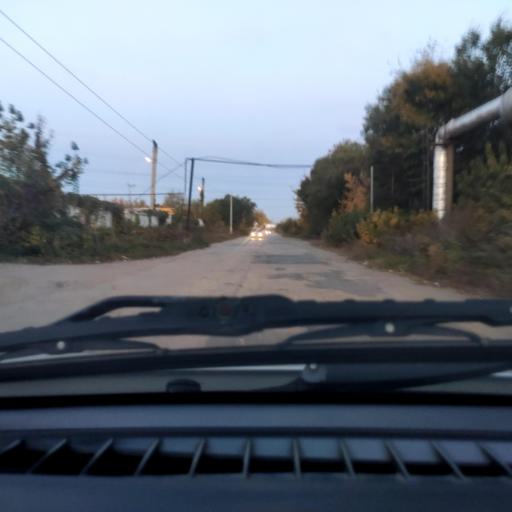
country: RU
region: Samara
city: Tol'yatti
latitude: 53.5472
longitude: 49.4464
